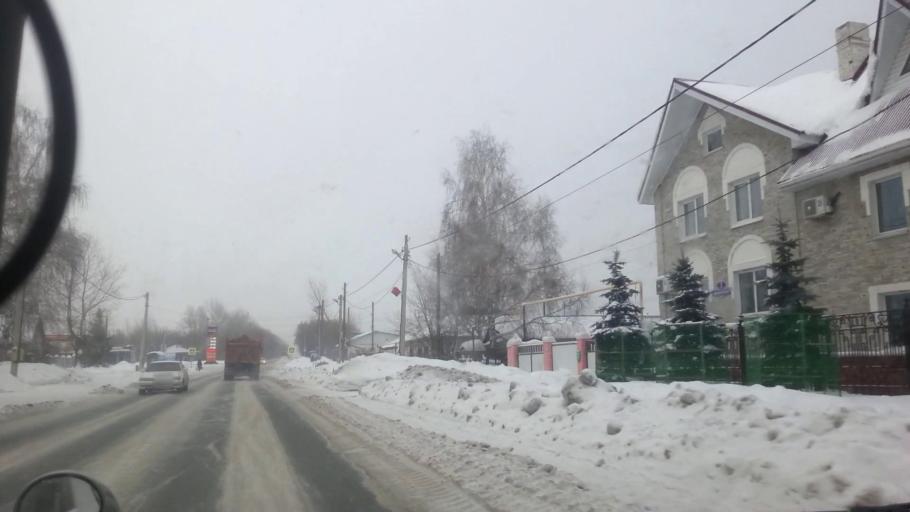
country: RU
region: Altai Krai
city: Vlasikha
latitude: 53.2990
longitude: 83.5899
